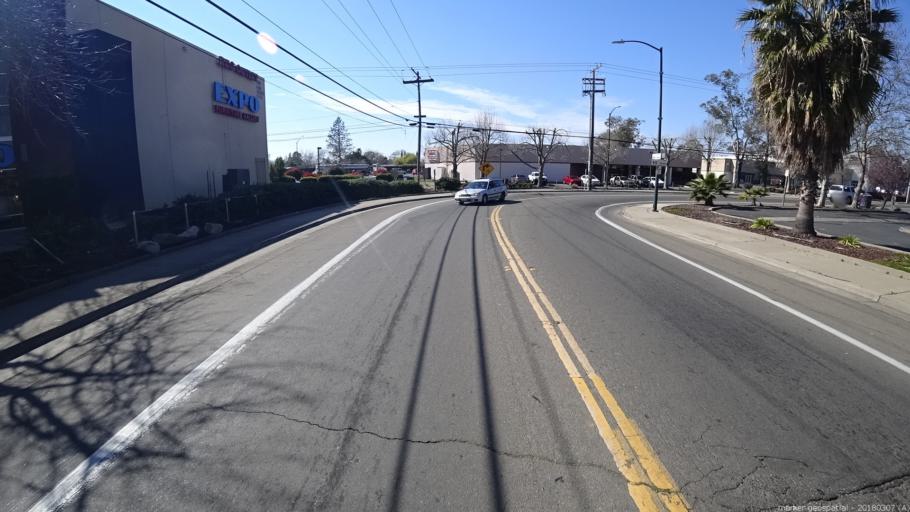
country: US
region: California
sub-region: Sacramento County
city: Parkway
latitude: 38.4924
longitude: -121.4408
